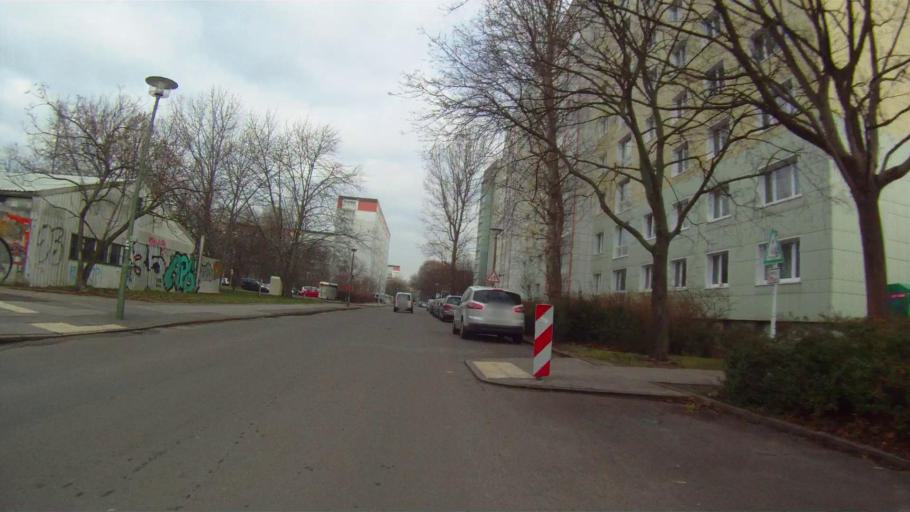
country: DE
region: Berlin
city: Friedrichsfelde
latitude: 52.4926
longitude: 13.5078
